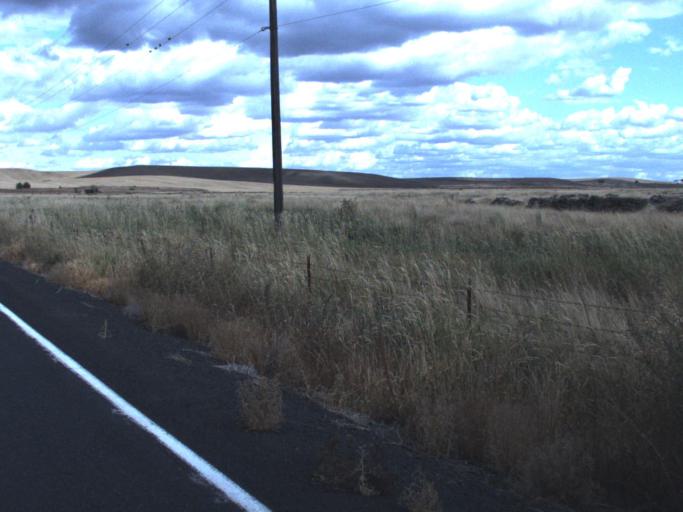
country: US
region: Washington
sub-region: Spokane County
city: Medical Lake
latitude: 47.5236
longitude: -117.9210
